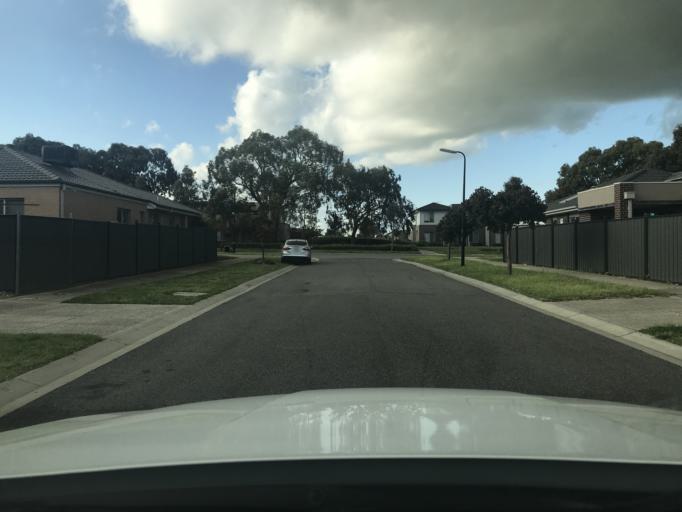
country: AU
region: Victoria
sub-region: Hume
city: Craigieburn
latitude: -37.5738
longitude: 144.9105
